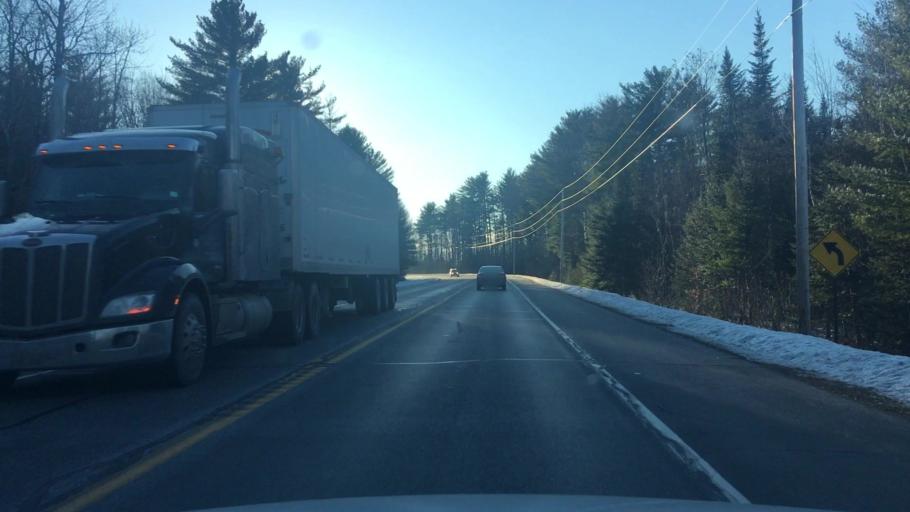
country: US
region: Maine
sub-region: Franklin County
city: New Sharon
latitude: 44.6670
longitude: -69.9503
